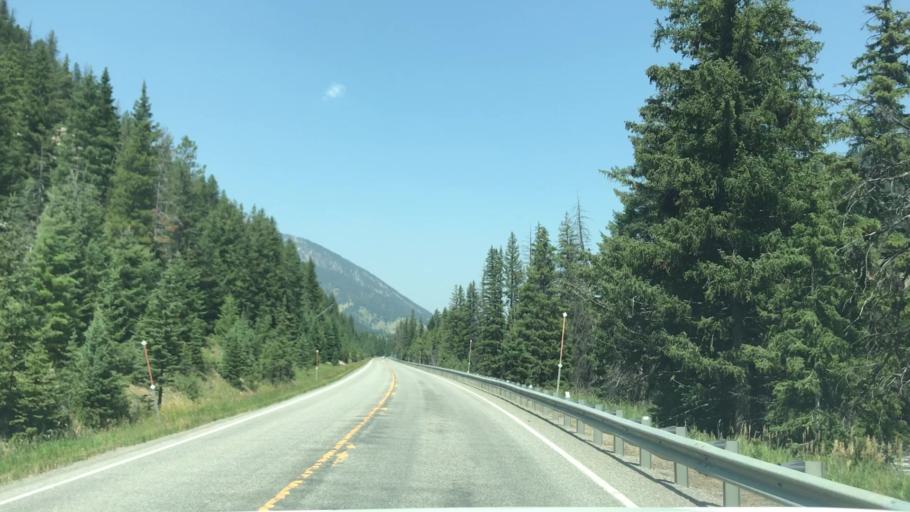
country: US
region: Montana
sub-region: Gallatin County
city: Big Sky
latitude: 45.0837
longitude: -111.2090
